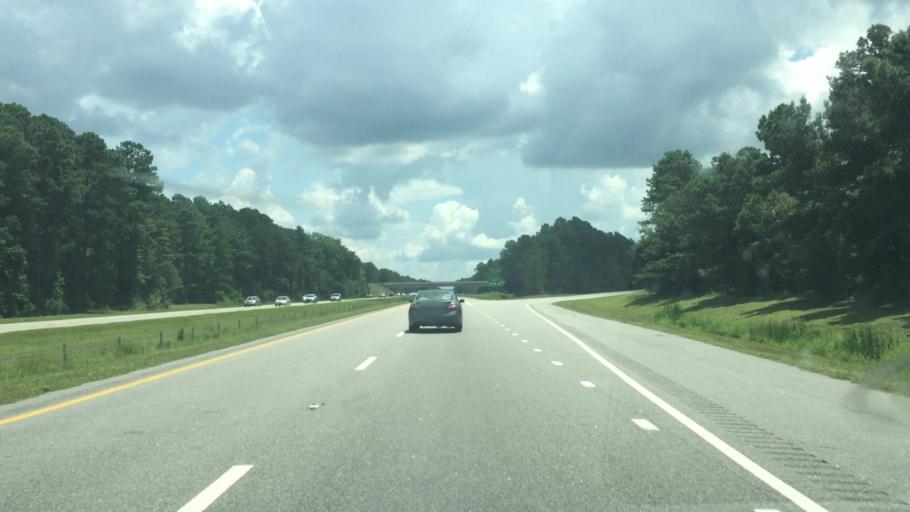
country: US
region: North Carolina
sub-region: Columbus County
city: Chadbourn
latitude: 34.3987
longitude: -78.9068
